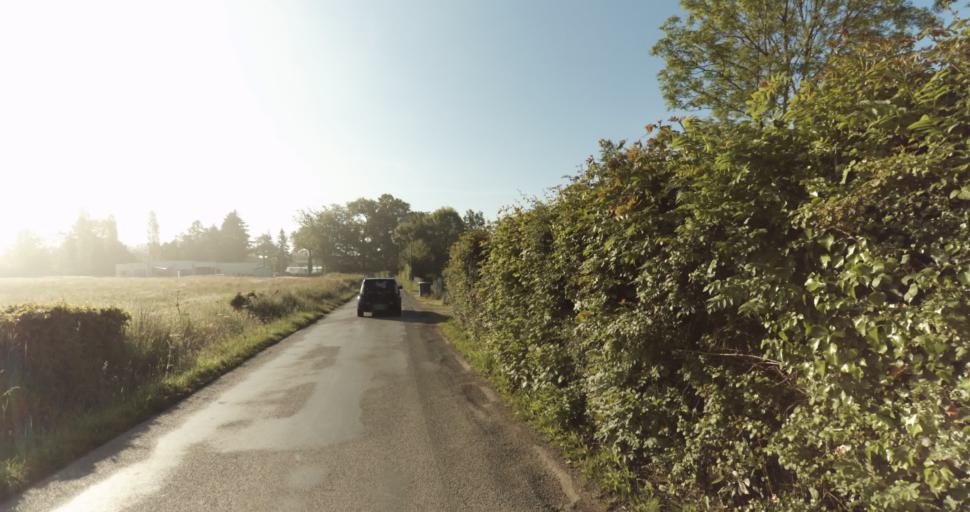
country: FR
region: Limousin
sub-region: Departement de la Haute-Vienne
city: Condat-sur-Vienne
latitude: 45.7825
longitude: 1.2841
